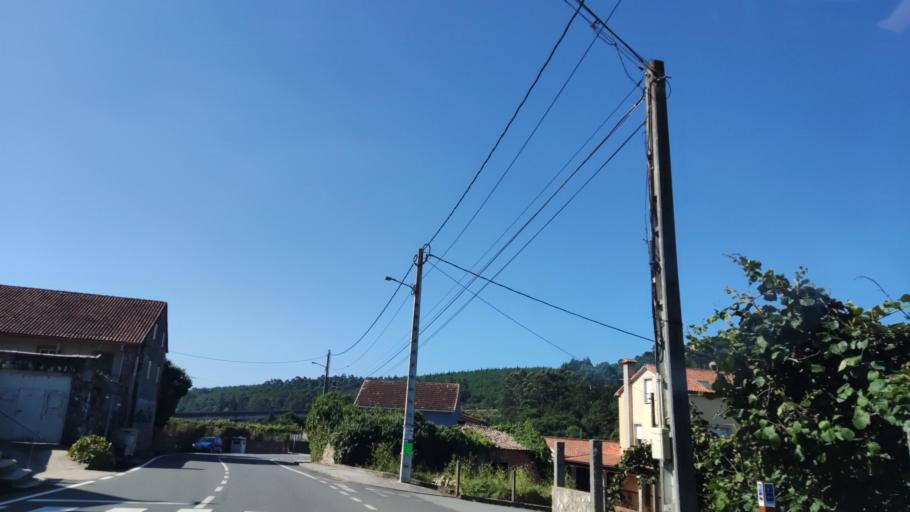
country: ES
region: Galicia
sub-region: Provincia da Coruna
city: Rianxo
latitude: 42.6762
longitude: -8.8552
